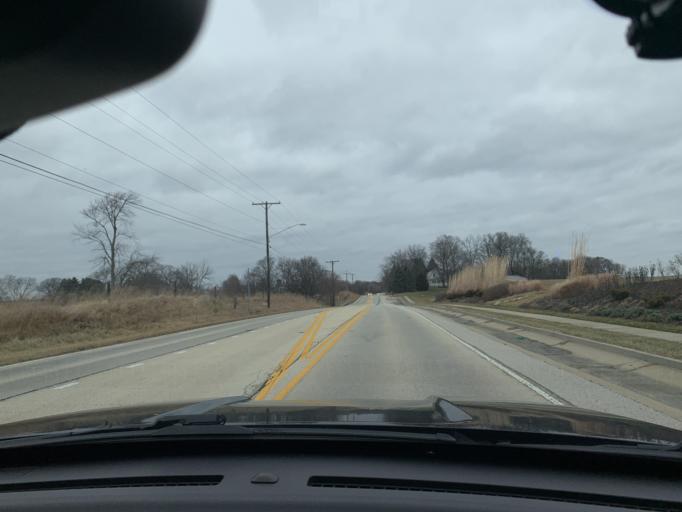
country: US
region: Illinois
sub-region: Sangamon County
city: Jerome
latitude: 39.7232
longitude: -89.6909
